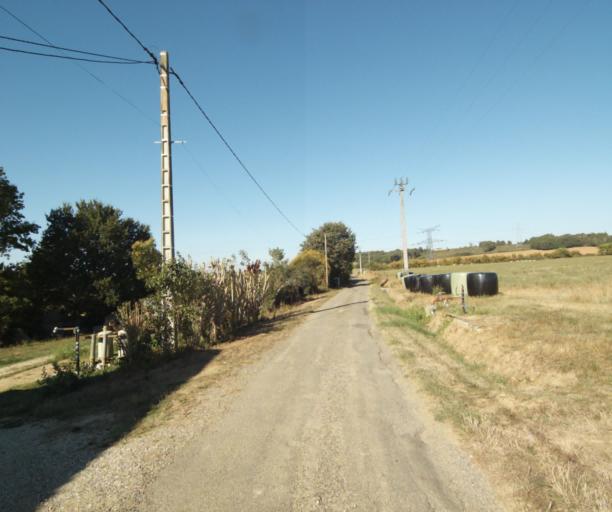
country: FR
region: Midi-Pyrenees
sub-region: Departement du Tarn-et-Garonne
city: Verdun-sur-Garonne
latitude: 43.8594
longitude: 1.1995
